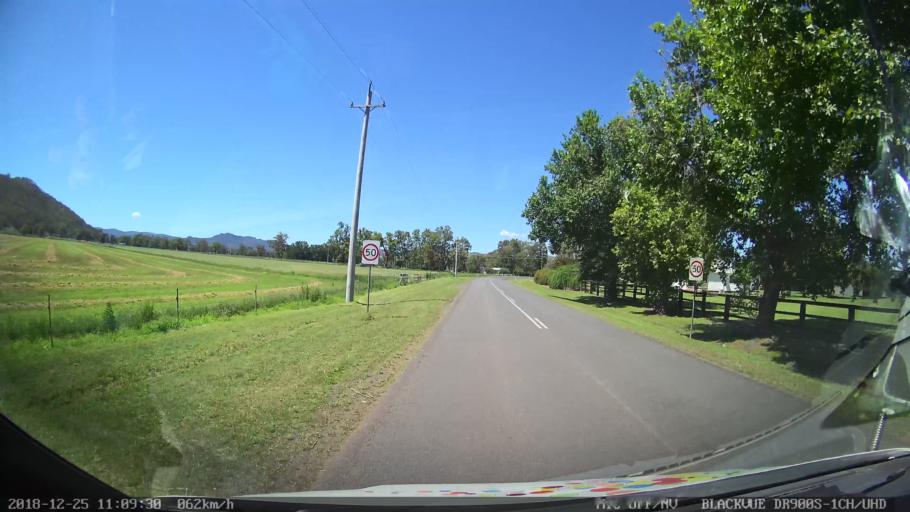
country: AU
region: New South Wales
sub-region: Upper Hunter Shire
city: Merriwa
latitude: -32.4118
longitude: 150.1185
